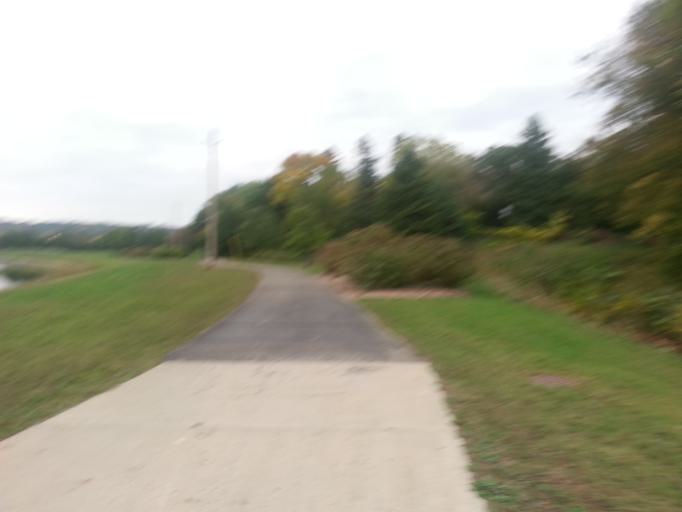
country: US
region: Minnesota
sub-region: Olmsted County
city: Rochester
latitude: 44.0273
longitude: -92.4589
